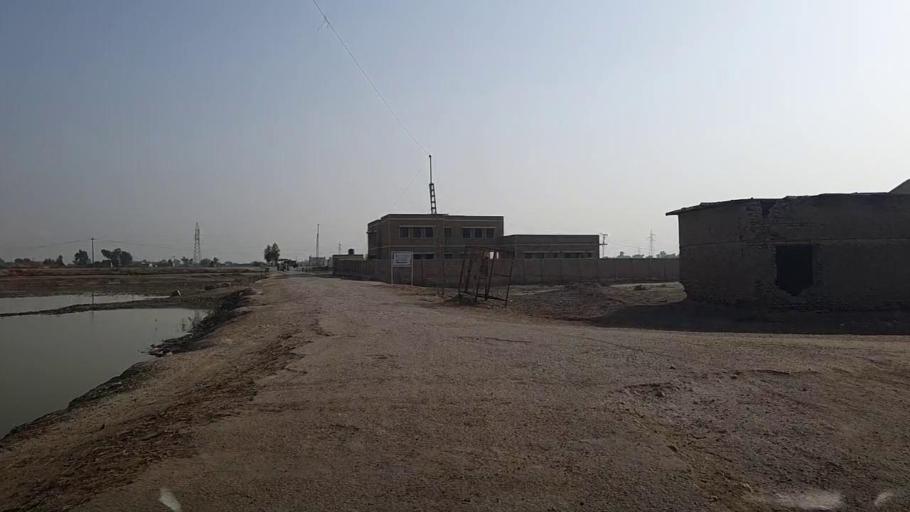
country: PK
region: Sindh
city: Kandhkot
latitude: 28.2772
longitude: 69.2548
